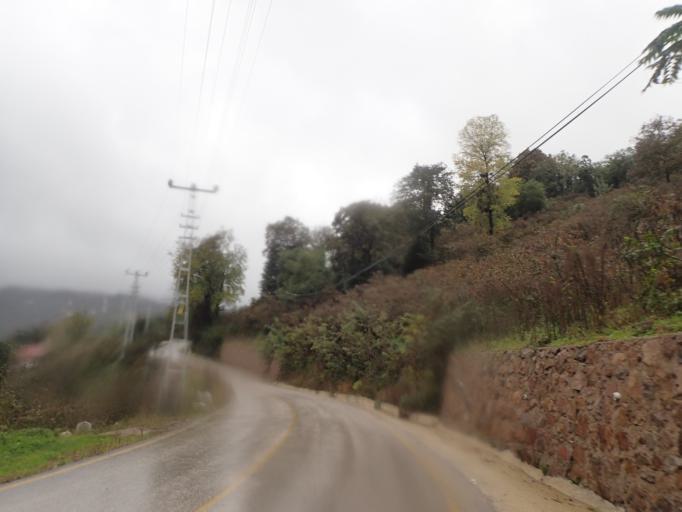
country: TR
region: Ordu
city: Persembe
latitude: 41.0421
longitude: 37.7362
